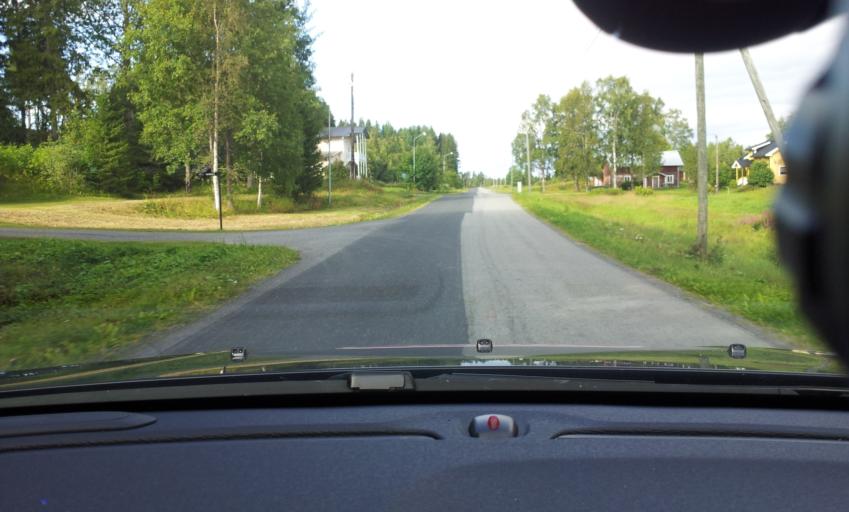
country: SE
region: Jaemtland
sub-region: Krokoms Kommun
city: Valla
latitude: 63.2730
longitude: 13.8927
